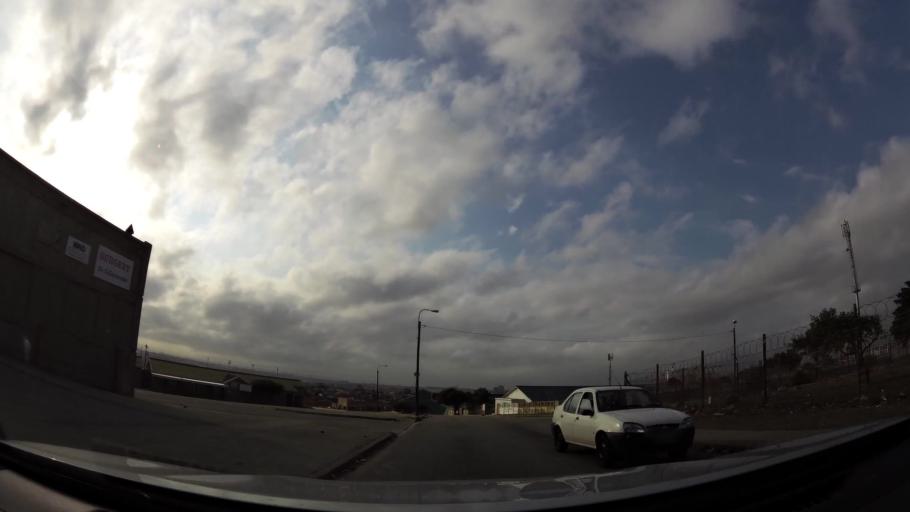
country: ZA
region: Eastern Cape
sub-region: Nelson Mandela Bay Metropolitan Municipality
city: Port Elizabeth
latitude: -33.9170
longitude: 25.5488
